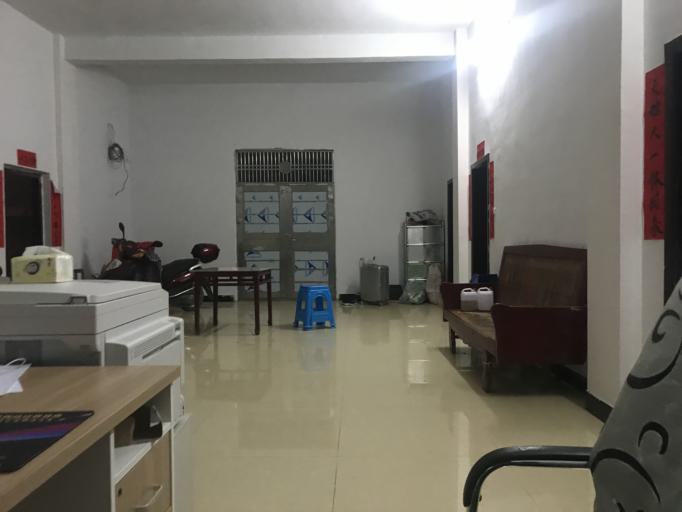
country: CN
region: Guizhou Sheng
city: Xujiaba
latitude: 27.9018
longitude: 108.1826
